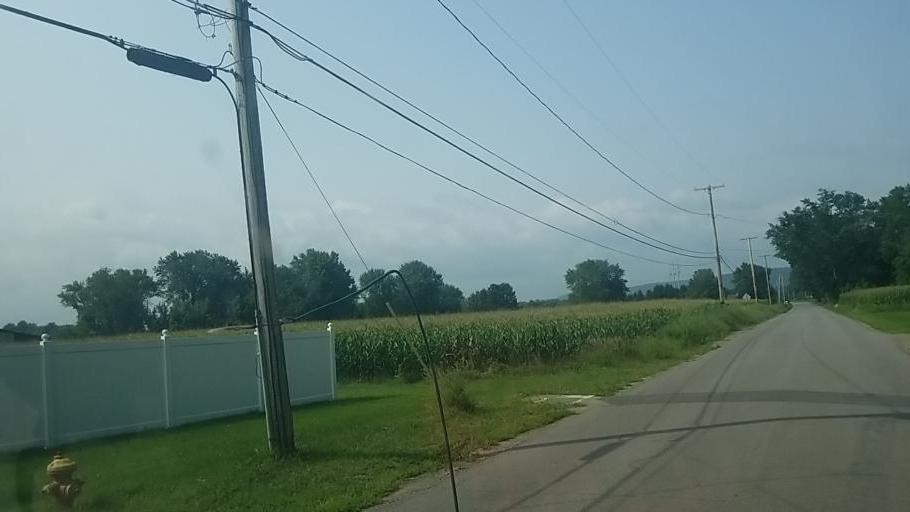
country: US
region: New York
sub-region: Montgomery County
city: Fonda
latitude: 42.9512
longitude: -74.4137
